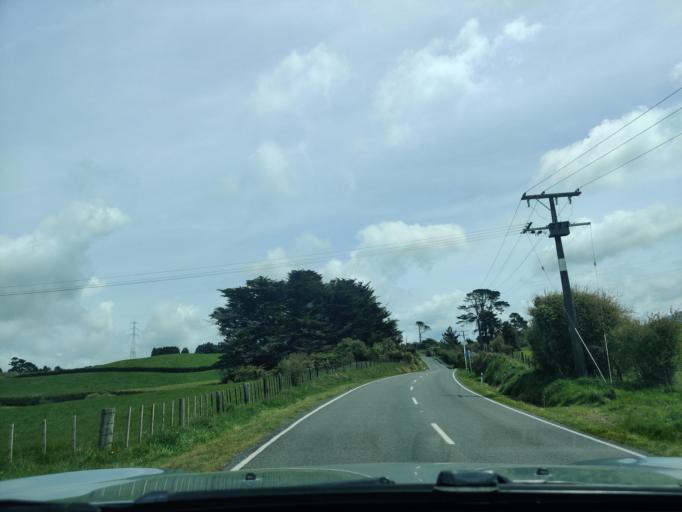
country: NZ
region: Taranaki
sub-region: South Taranaki District
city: Eltham
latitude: -39.3754
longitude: 174.1864
